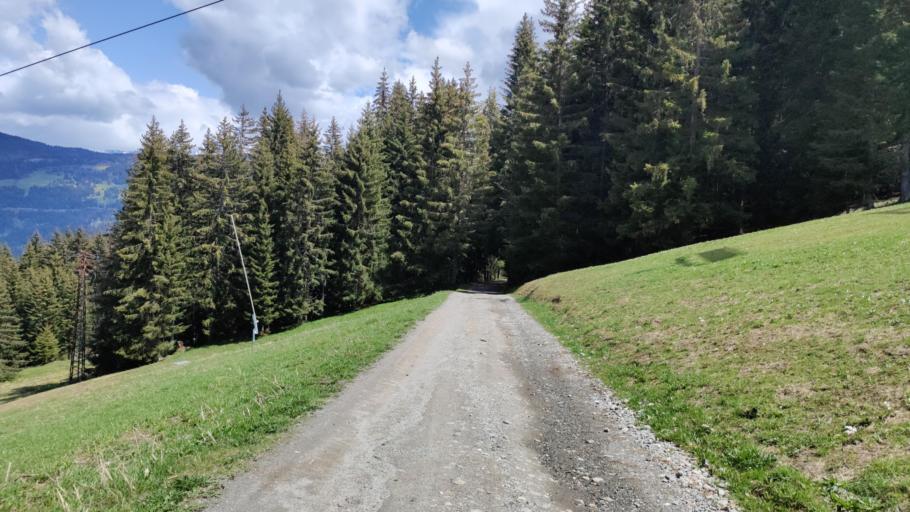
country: FR
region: Rhone-Alpes
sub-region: Departement de la Haute-Savoie
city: Saint-Gervais-les-Bains
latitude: 45.8773
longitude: 6.6777
